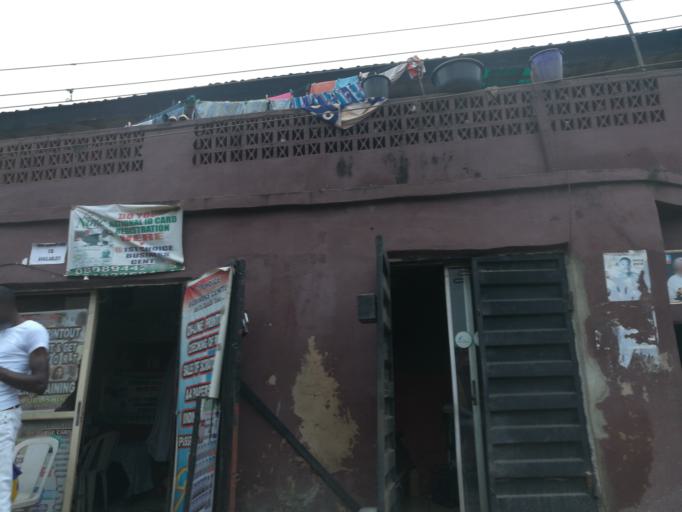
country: NG
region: Lagos
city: Makoko
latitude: 6.4965
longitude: 3.3868
